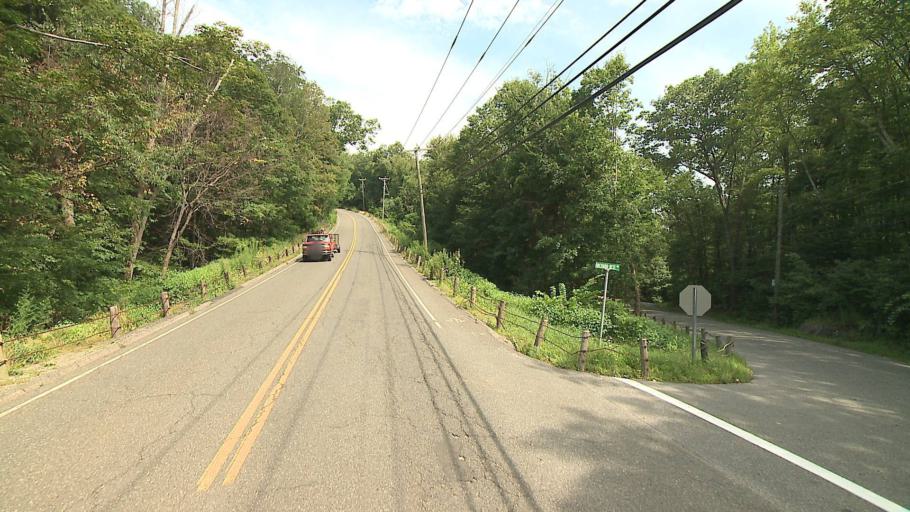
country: US
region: Connecticut
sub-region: Fairfield County
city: Sherman
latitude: 41.5503
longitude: -73.4820
